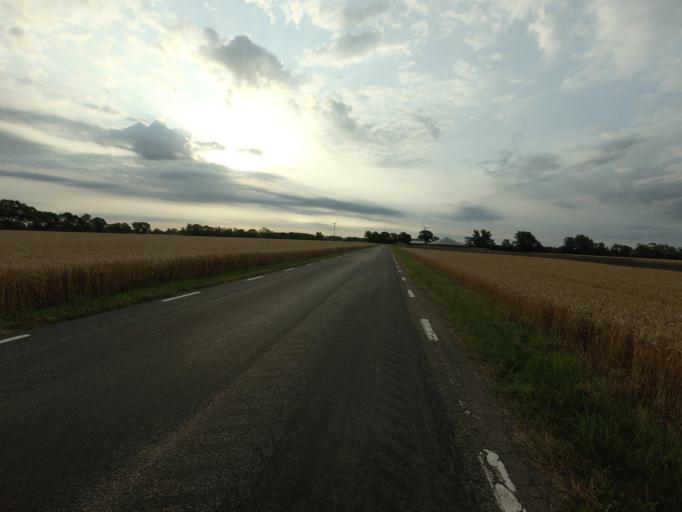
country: SE
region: Skane
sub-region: Hoganas Kommun
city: Hoganas
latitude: 56.1528
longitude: 12.6375
